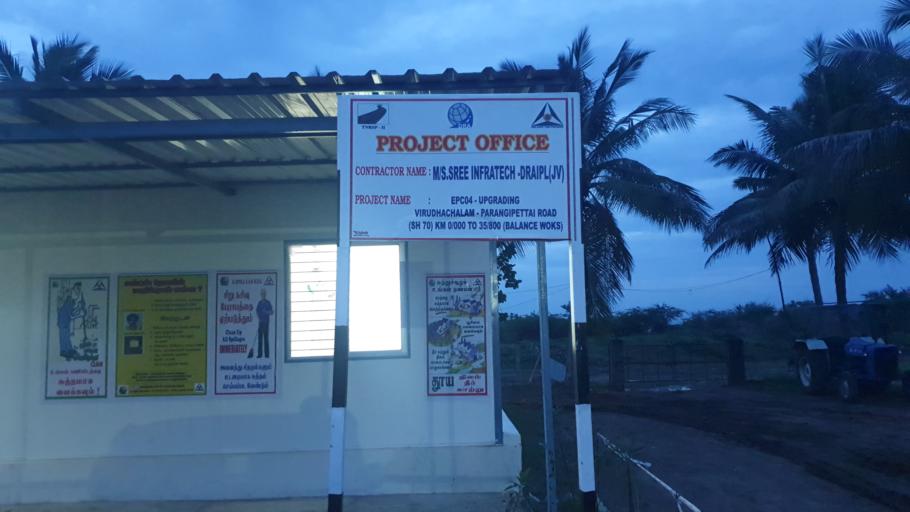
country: IN
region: Tamil Nadu
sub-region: Cuddalore
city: Bhuvanagiri
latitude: 11.4496
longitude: 79.5574
